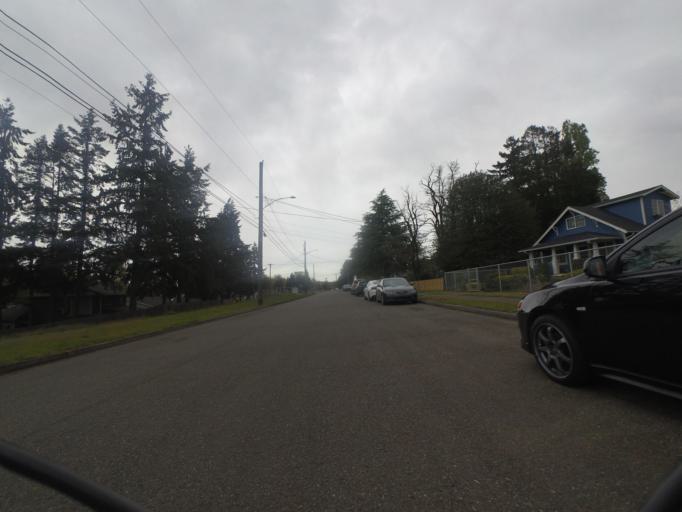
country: US
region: Washington
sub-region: Pierce County
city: Lakewood
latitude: 47.1983
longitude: -122.4760
